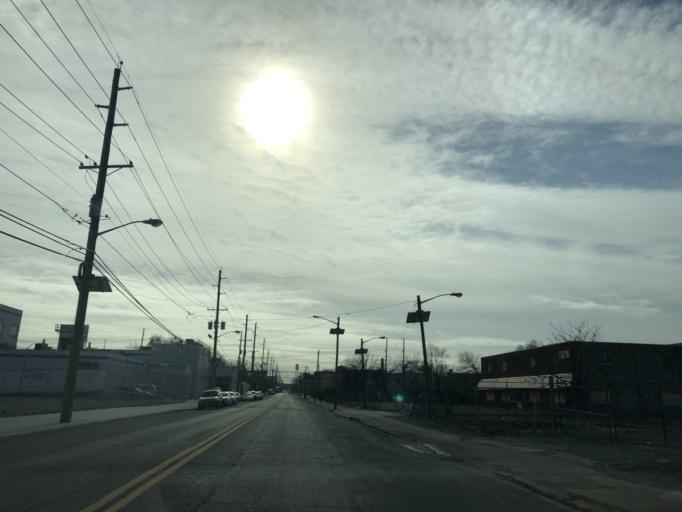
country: US
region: New Jersey
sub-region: Camden County
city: Camden
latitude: 39.9262
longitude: -75.1196
